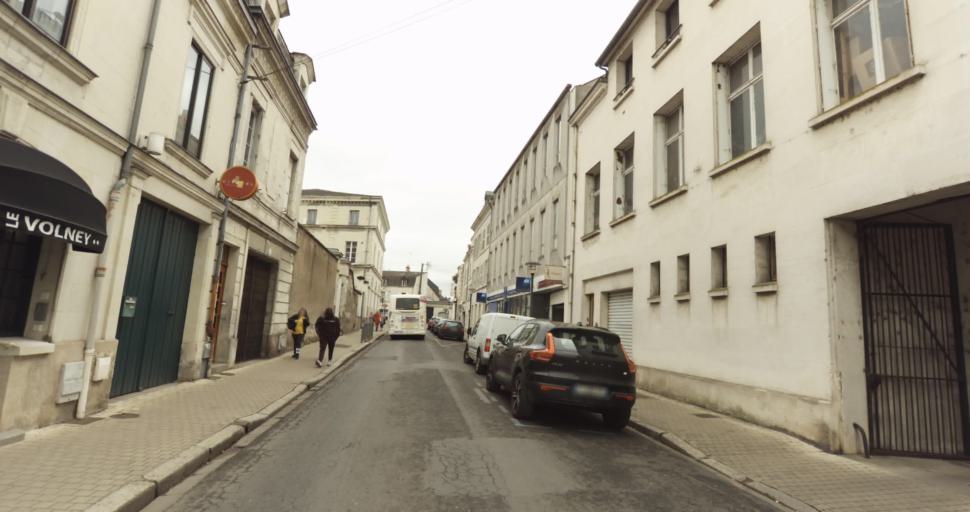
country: FR
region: Pays de la Loire
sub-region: Departement de Maine-et-Loire
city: Saumur
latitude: 47.2573
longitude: -0.0790
